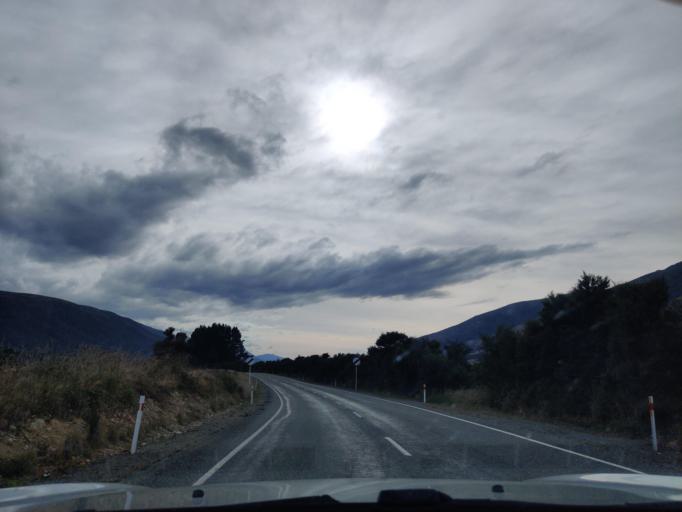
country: NZ
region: Tasman
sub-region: Tasman District
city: Wakefield
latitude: -41.7647
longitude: 172.9738
